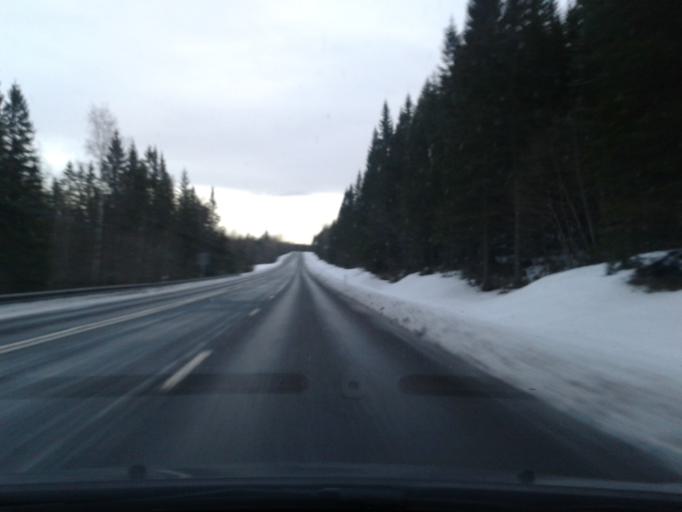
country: SE
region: Vaesternorrland
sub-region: Solleftea Kommun
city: Solleftea
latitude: 63.1356
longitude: 17.4532
